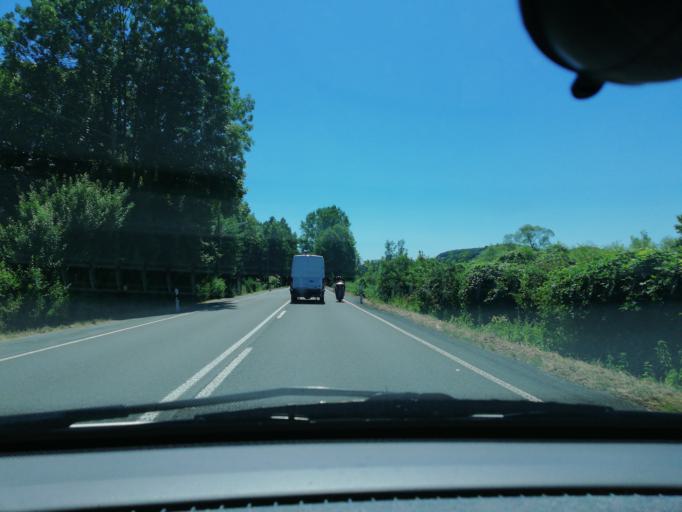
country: DE
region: North Rhine-Westphalia
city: Witten
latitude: 51.4096
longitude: 7.3533
